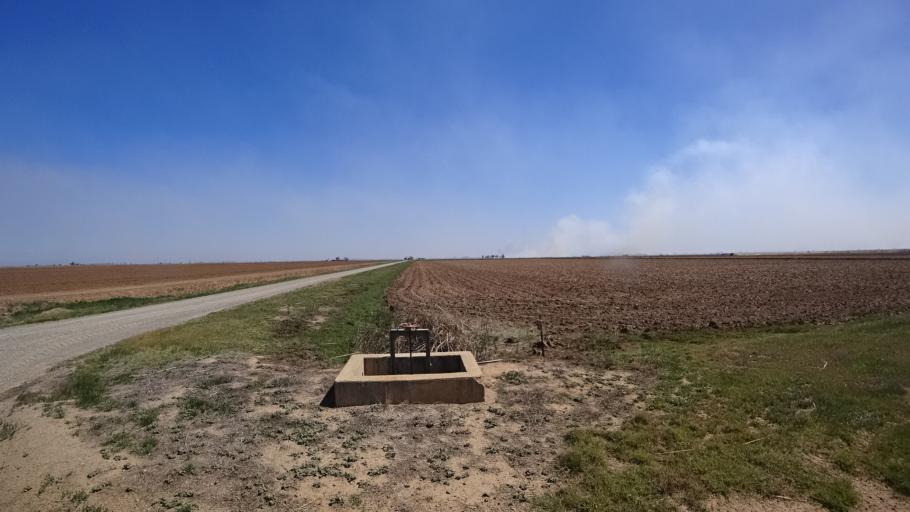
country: US
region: California
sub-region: Colusa County
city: Maxwell
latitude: 39.3850
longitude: -122.2482
